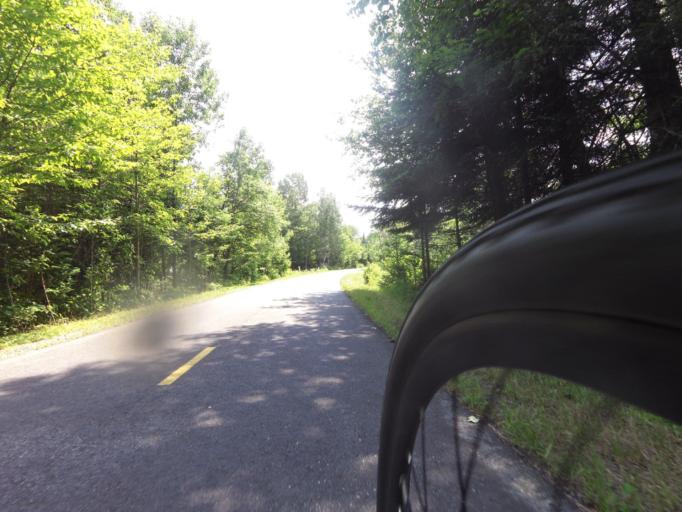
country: CA
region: Quebec
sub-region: Laurentides
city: Mont-Tremblant
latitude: 46.1594
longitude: -74.6003
